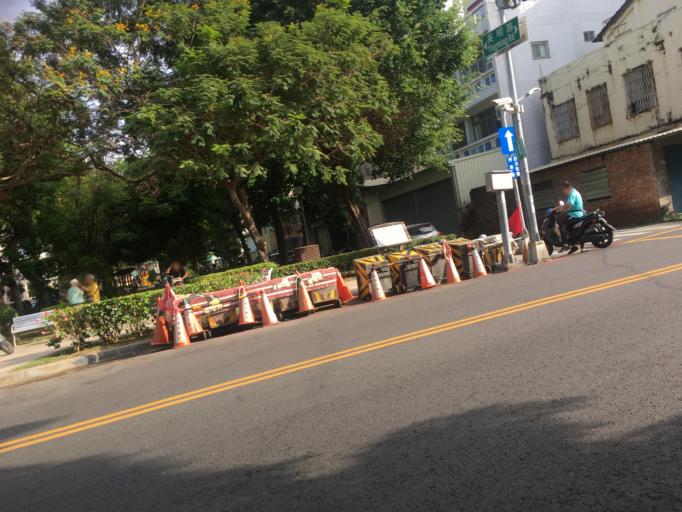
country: TW
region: Kaohsiung
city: Kaohsiung
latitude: 22.6215
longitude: 120.3228
